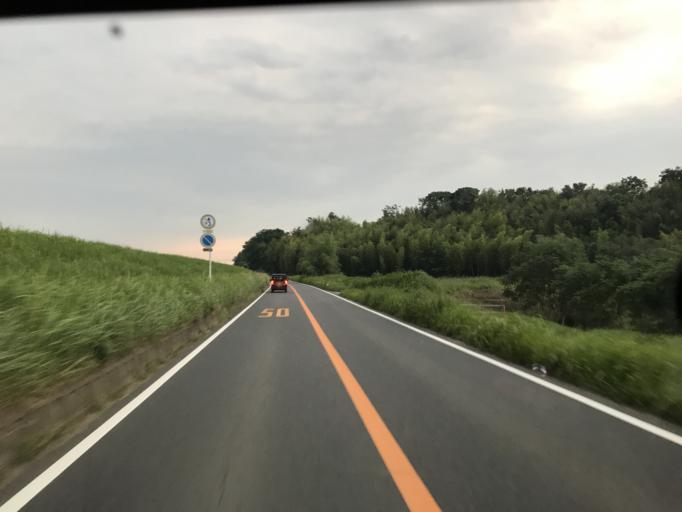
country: JP
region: Ibaraki
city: Fujishiro
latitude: 35.8600
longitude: 140.1302
